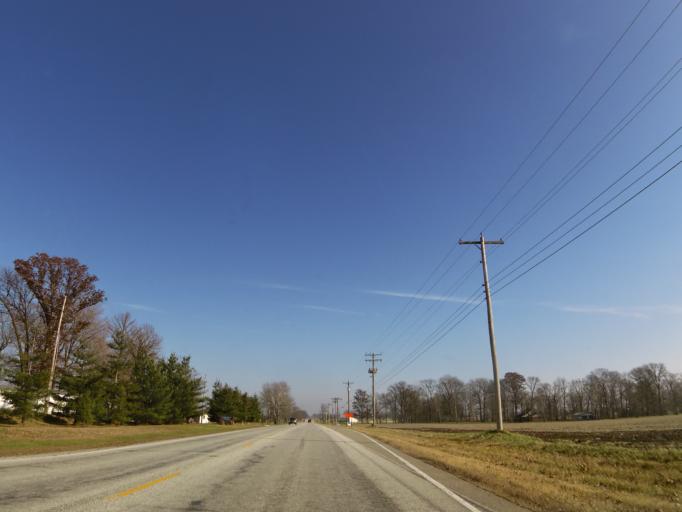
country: US
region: Indiana
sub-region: Shelby County
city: Shelbyville
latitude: 39.5315
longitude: -85.7240
